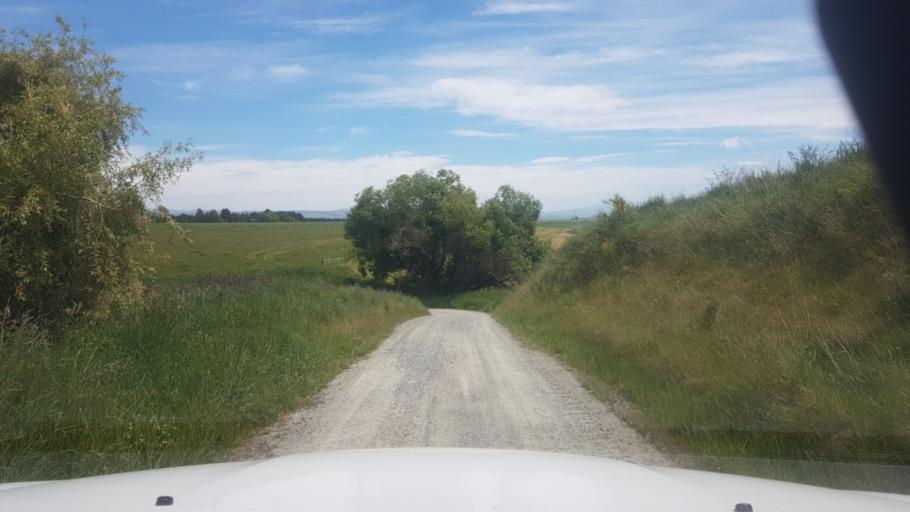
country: NZ
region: Canterbury
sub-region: Timaru District
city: Pleasant Point
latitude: -44.2144
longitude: 171.0533
